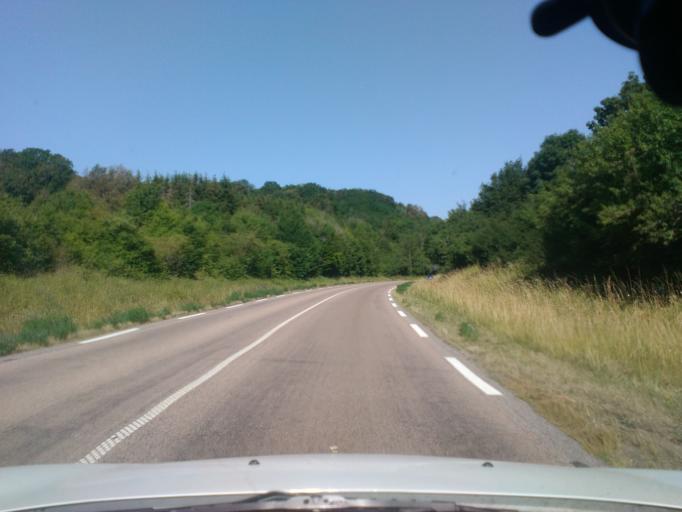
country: FR
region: Lorraine
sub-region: Departement des Vosges
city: Mirecourt
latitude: 48.3064
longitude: 6.0334
